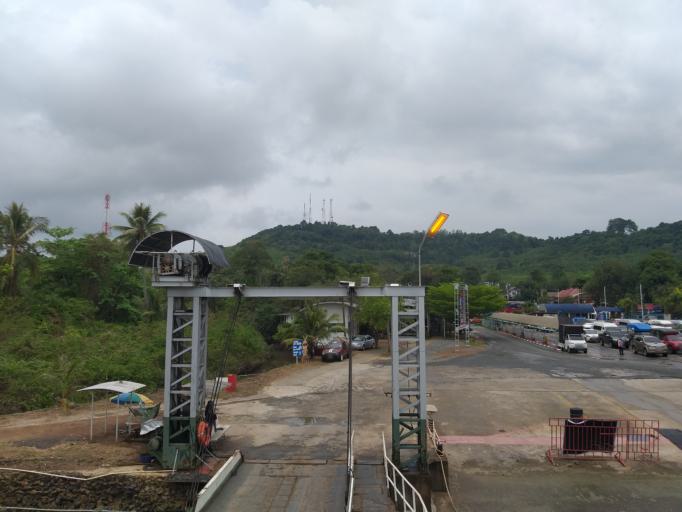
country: TH
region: Trat
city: Laem Ngop
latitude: 12.1870
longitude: 102.3011
